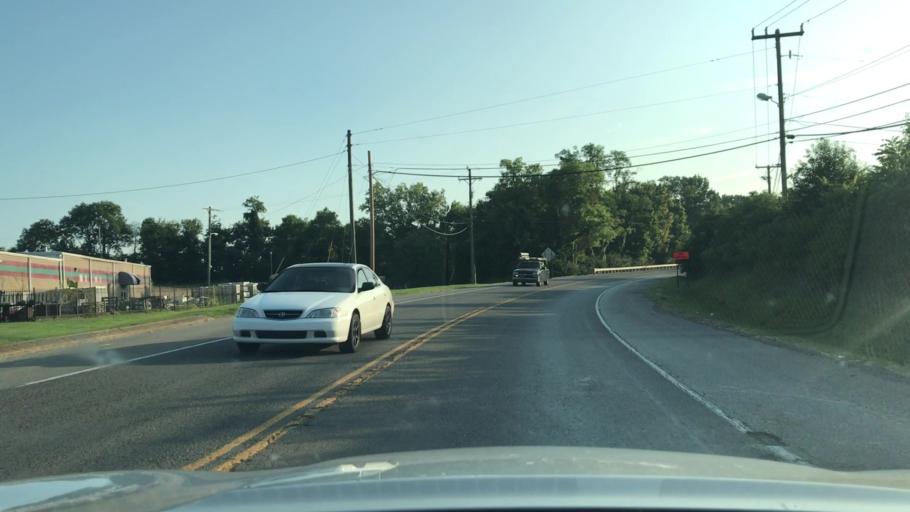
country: US
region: Tennessee
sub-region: Rutherford County
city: La Vergne
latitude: 36.0184
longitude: -86.6195
